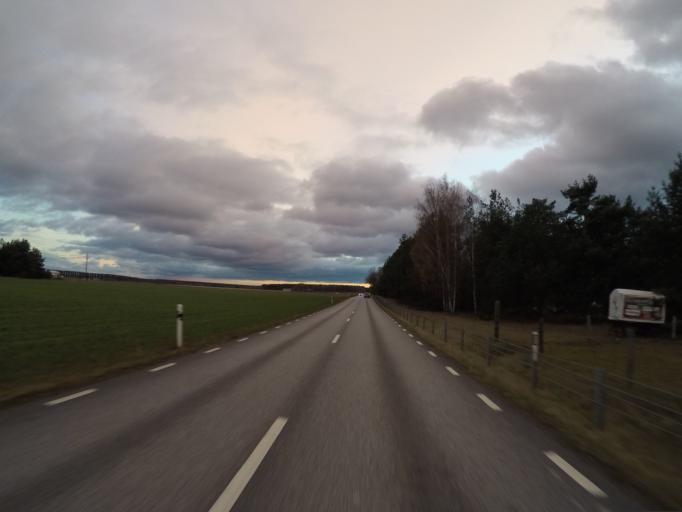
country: SE
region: Skane
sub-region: Kristianstads Kommun
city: Norra Asum
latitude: 55.9286
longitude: 14.0747
